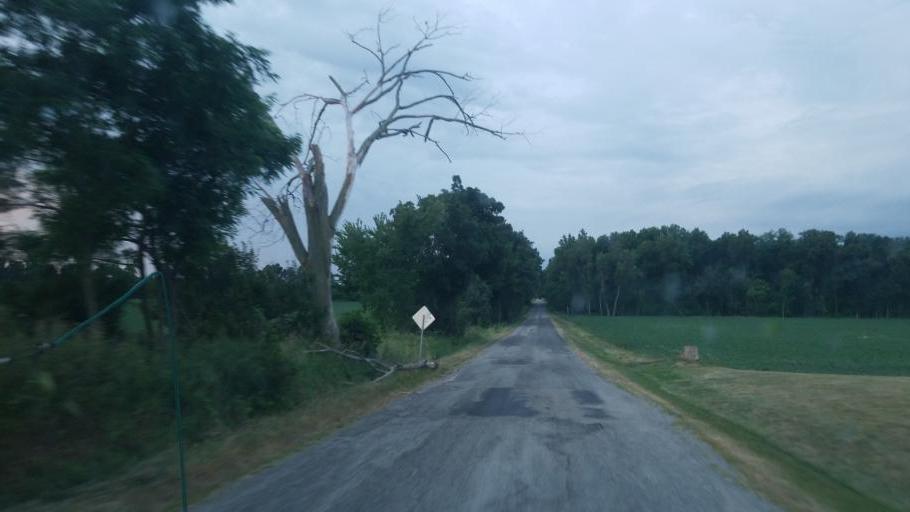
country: US
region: Ohio
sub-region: Defiance County
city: Hicksville
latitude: 41.3389
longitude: -84.8304
